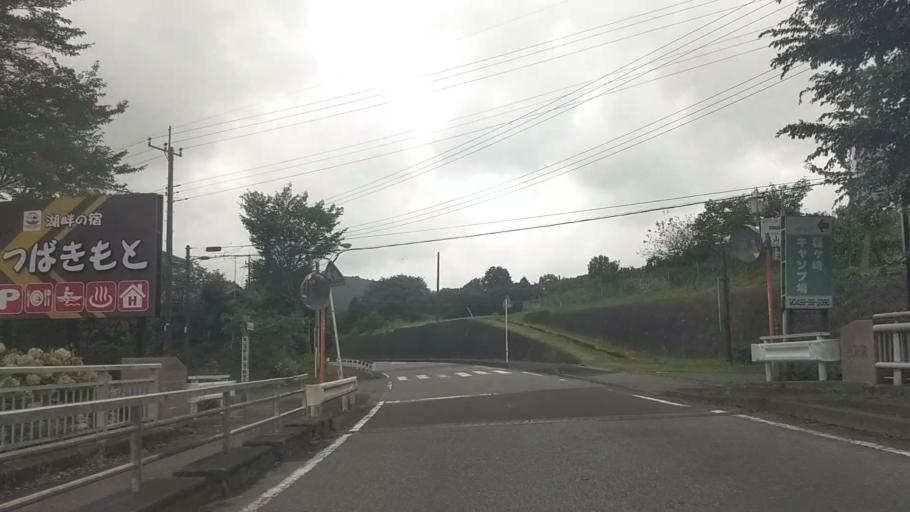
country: JP
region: Chiba
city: Kawaguchi
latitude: 35.2285
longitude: 140.0987
